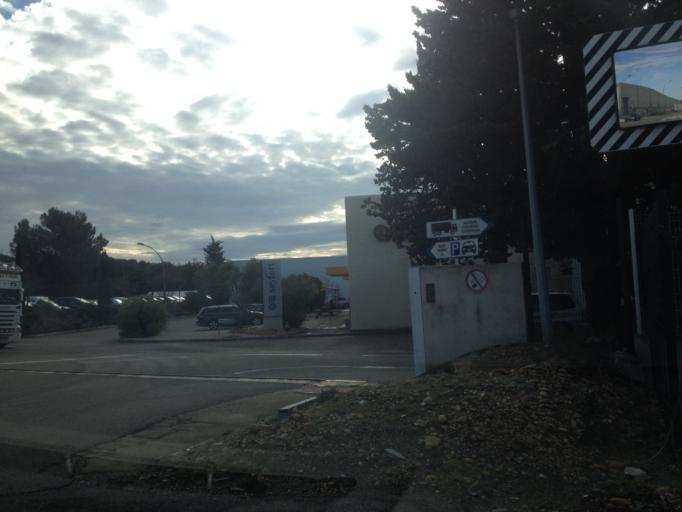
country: FR
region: Provence-Alpes-Cote d'Azur
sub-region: Departement du Vaucluse
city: Sorgues
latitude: 44.0116
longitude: 4.8891
